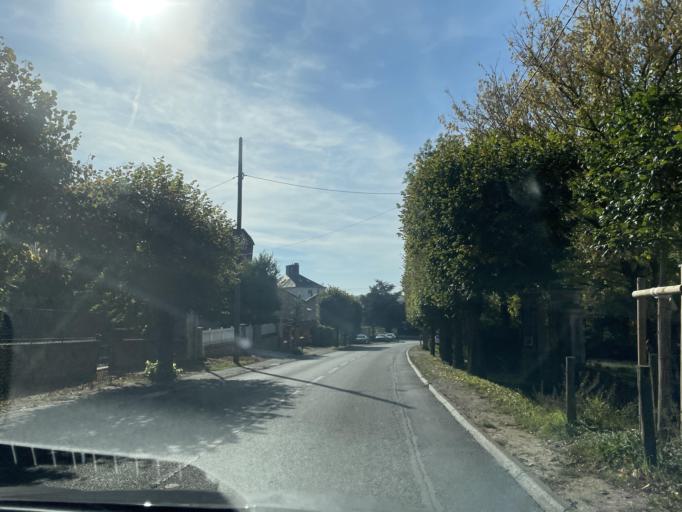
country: FR
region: Ile-de-France
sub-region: Departement de Seine-et-Marne
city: Coulommiers
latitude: 48.8194
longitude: 3.0884
